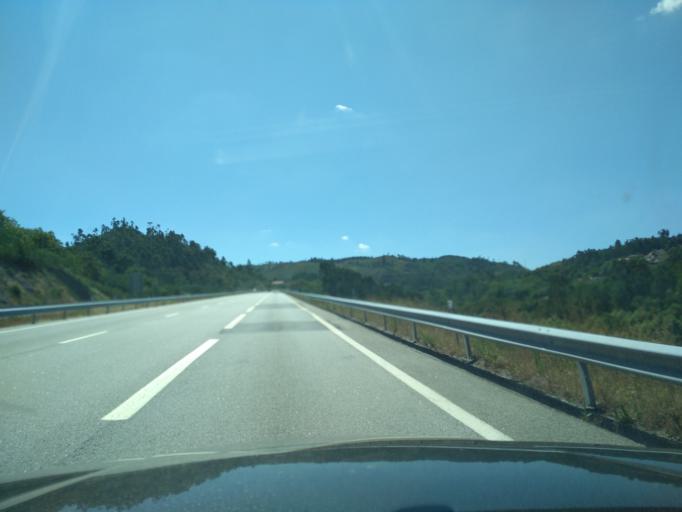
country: PT
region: Braga
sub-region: Celorico de Basto
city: Celorico de Basto
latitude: 41.4510
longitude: -8.0482
